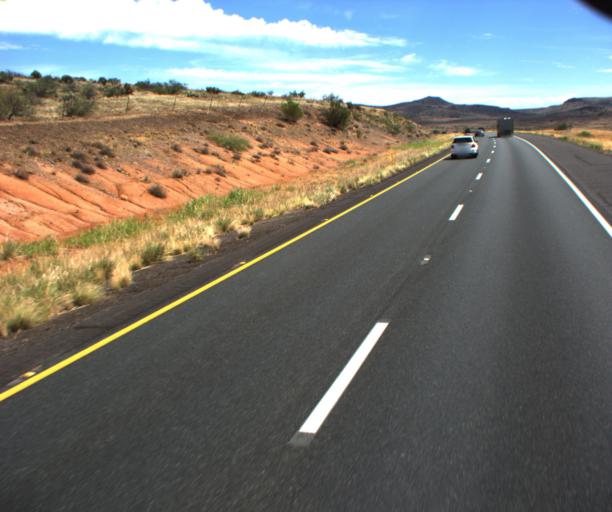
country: US
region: Arizona
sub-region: Yavapai County
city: Cordes Lakes
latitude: 34.4276
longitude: -112.0374
